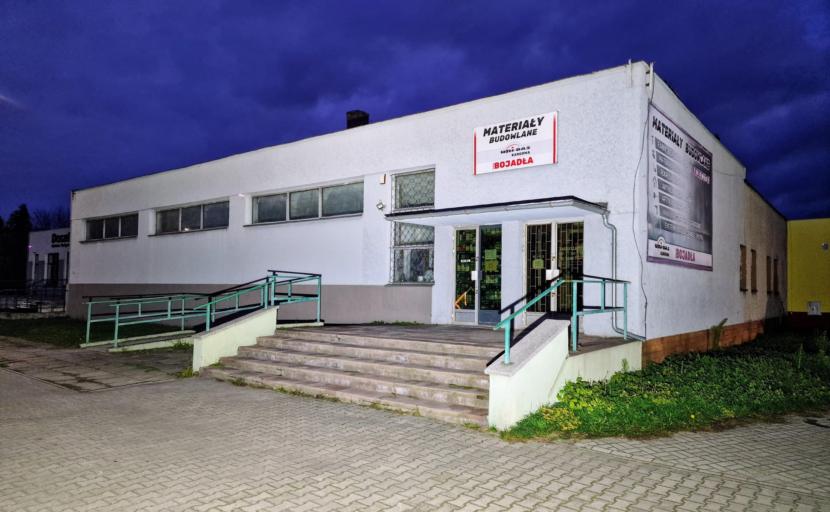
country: PL
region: Lubusz
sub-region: Powiat zielonogorski
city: Bojadla
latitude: 51.9529
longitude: 15.8096
